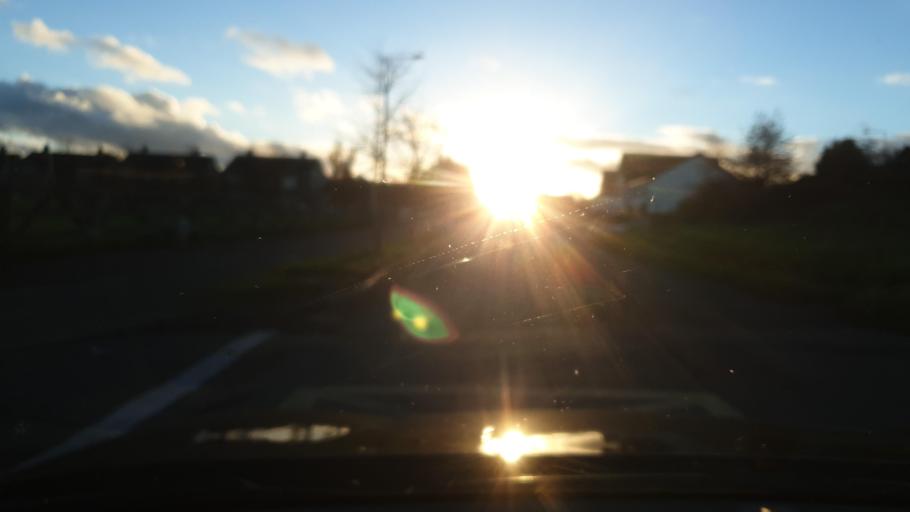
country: IE
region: Leinster
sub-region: Lu
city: Drogheda
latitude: 53.7256
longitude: -6.3291
